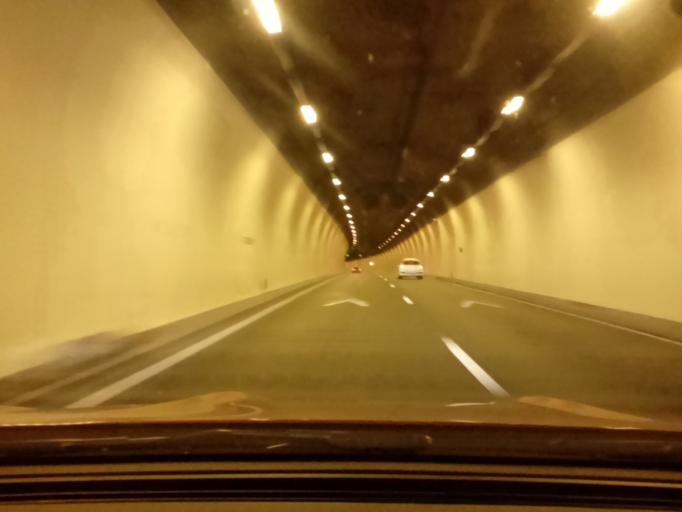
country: FR
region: Rhone-Alpes
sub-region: Departement du Rhone
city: Caluire-et-Cuire
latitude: 45.7903
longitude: 4.8113
